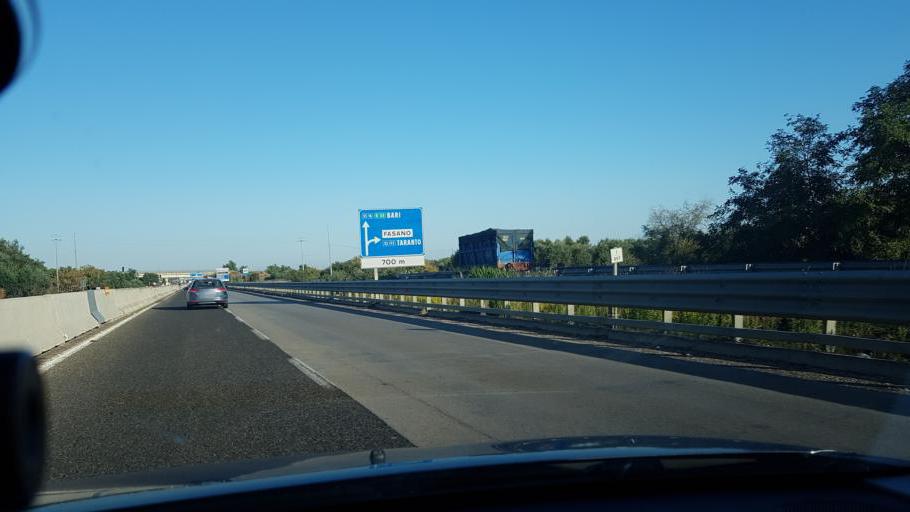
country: IT
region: Apulia
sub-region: Provincia di Brindisi
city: Fasano
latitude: 40.8476
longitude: 17.3610
